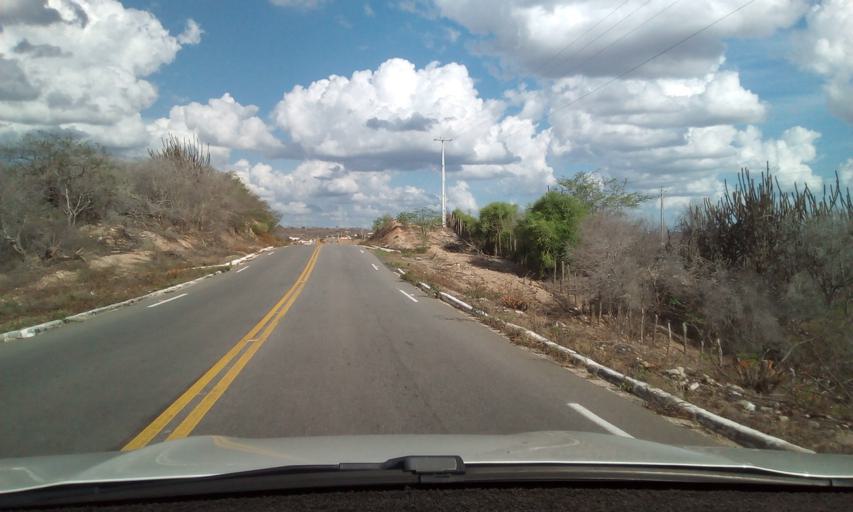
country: BR
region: Rio Grande do Norte
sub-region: Parelhas
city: Parelhas
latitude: -6.7947
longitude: -36.4164
